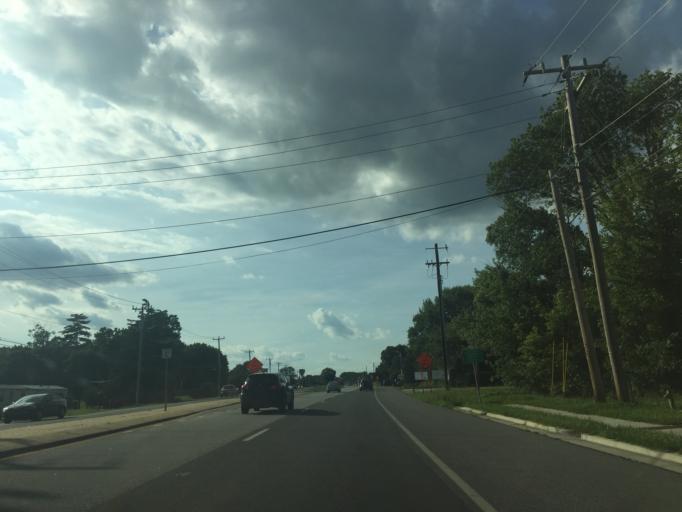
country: US
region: Delaware
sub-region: Kent County
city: Smyrna
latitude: 39.3098
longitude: -75.6101
